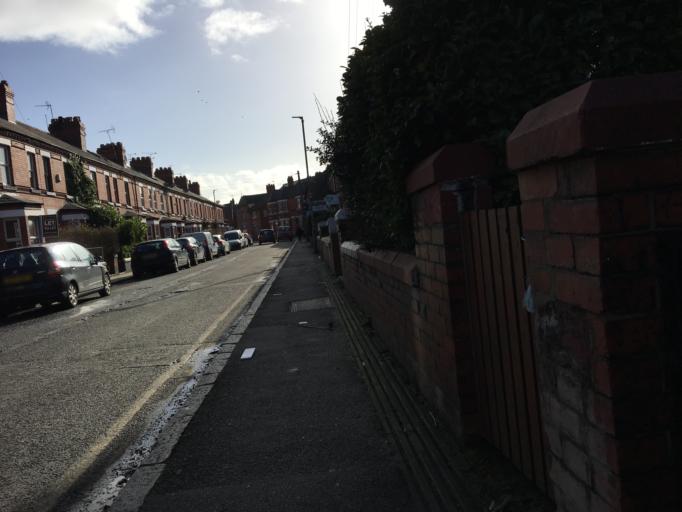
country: GB
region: England
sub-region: Cheshire West and Chester
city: Hoole
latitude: 53.1999
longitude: -2.8824
